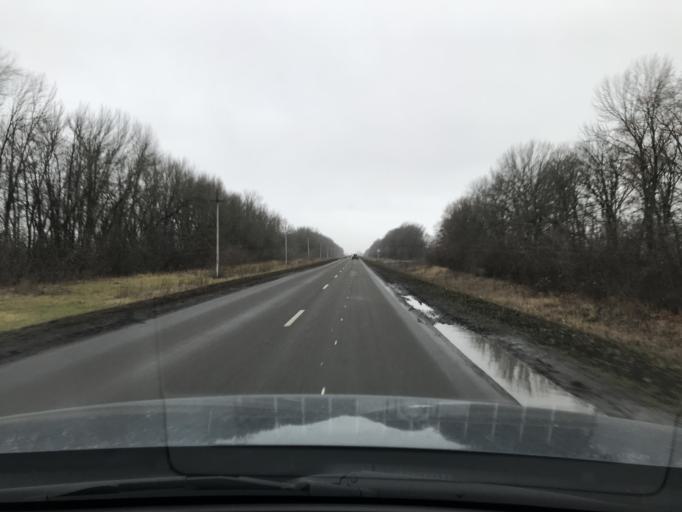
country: RU
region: Penza
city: Zemetchino
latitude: 53.5206
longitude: 42.6499
